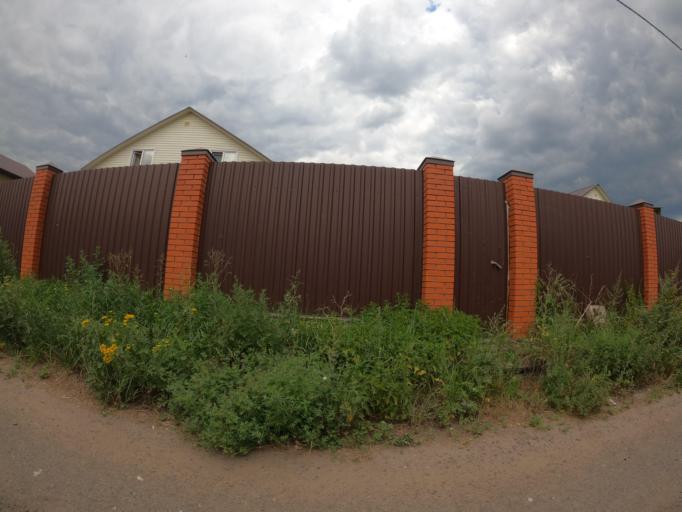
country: RU
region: Moskovskaya
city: Ramenskoye
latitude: 55.5401
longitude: 38.2300
